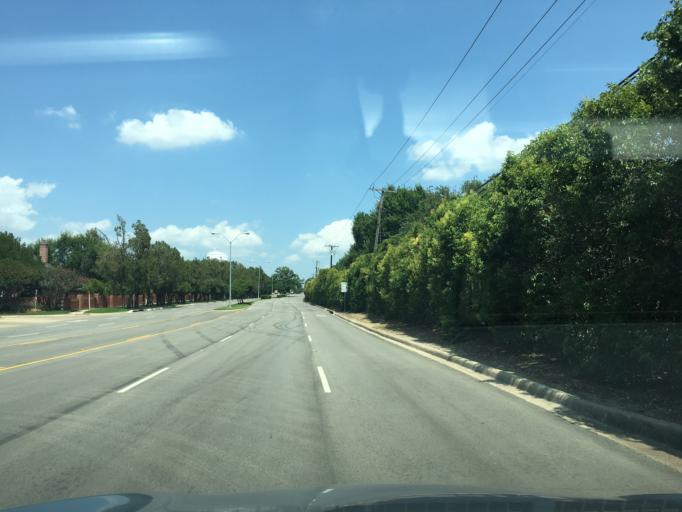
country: US
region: Texas
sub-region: Dallas County
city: Farmers Branch
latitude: 32.9241
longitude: -96.8610
